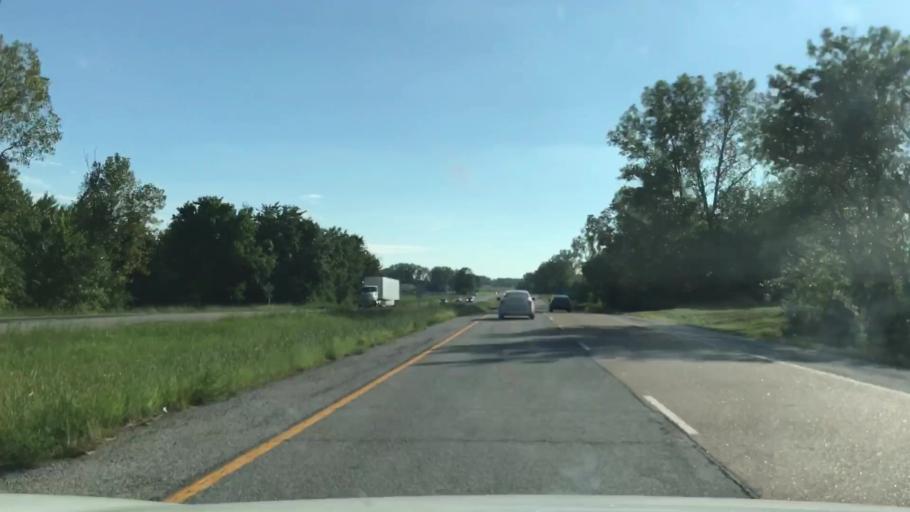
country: US
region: Illinois
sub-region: Madison County
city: Mitchell
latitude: 38.7766
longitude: -90.1147
